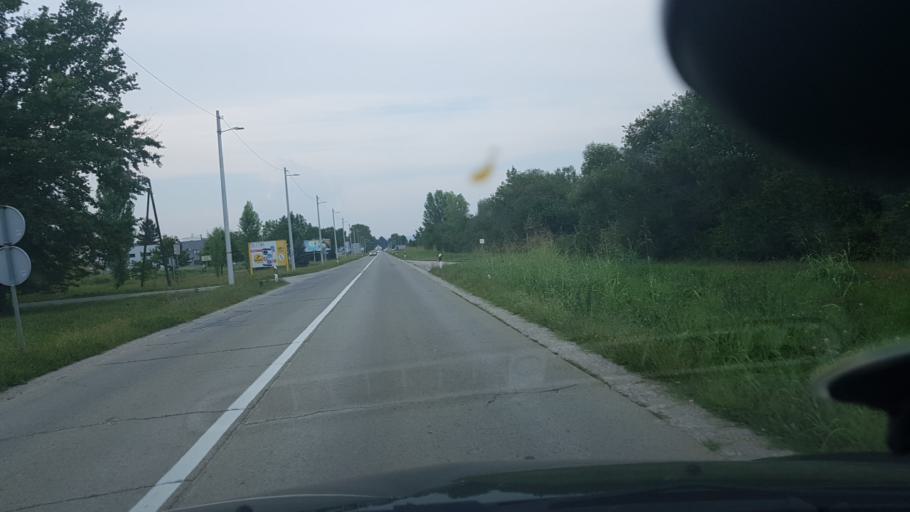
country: HR
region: Zagrebacka
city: Bregana
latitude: 45.8263
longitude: 15.7024
